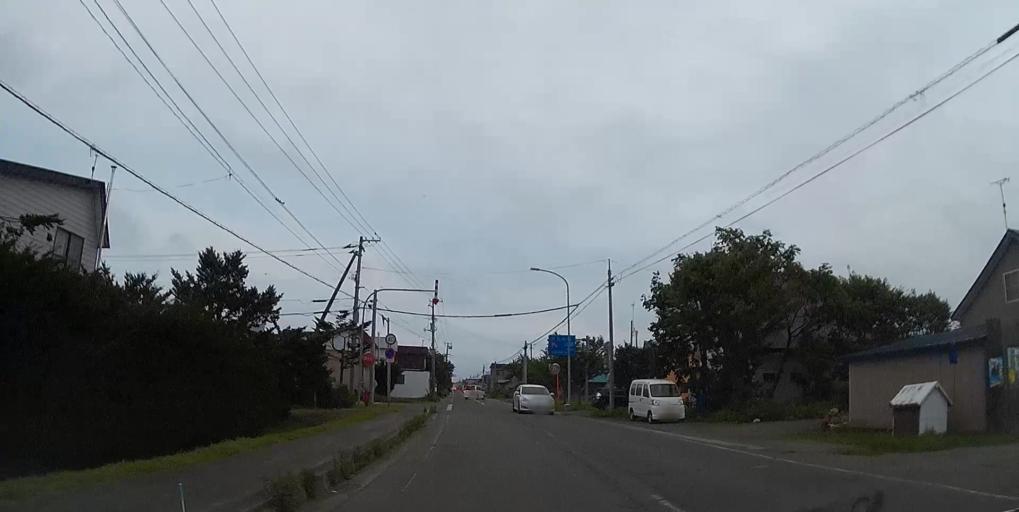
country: JP
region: Hokkaido
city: Nanae
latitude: 42.2540
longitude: 140.2565
